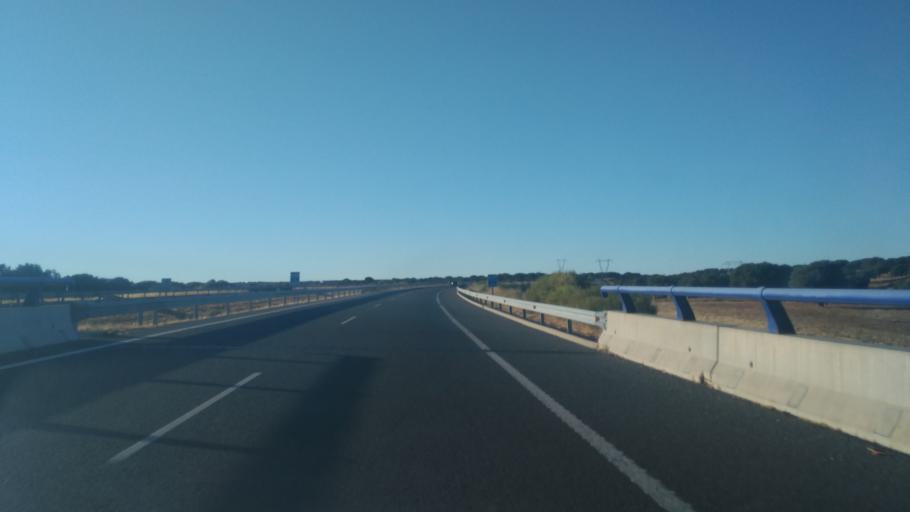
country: ES
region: Castille and Leon
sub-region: Provincia de Salamanca
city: Belena
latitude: 40.7260
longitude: -5.6328
